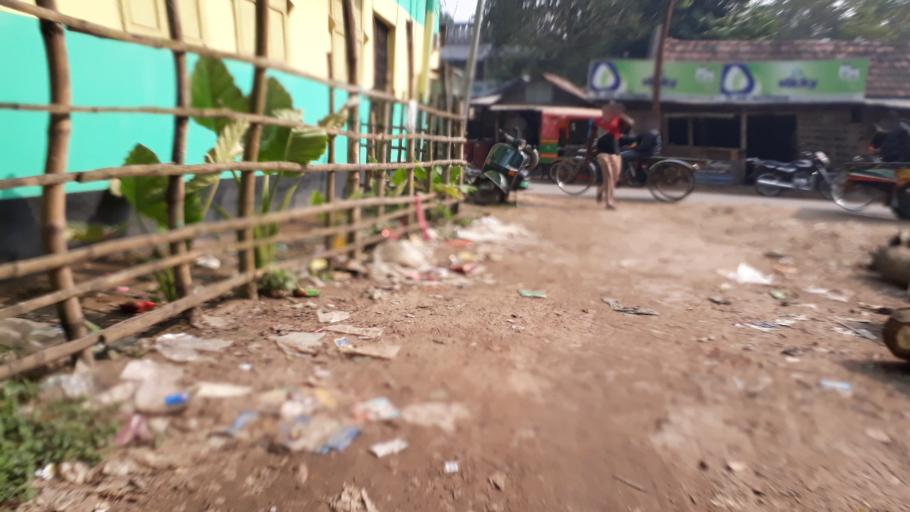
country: BD
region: Khulna
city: Kaliganj
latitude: 23.3538
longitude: 88.9145
